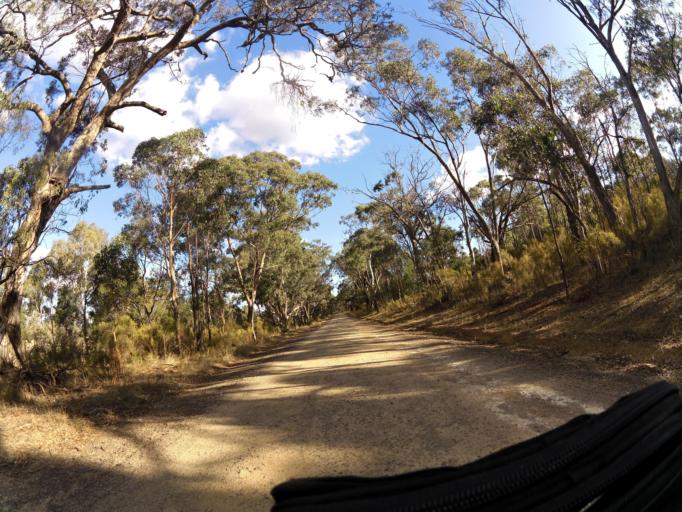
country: AU
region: Victoria
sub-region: Greater Bendigo
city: Kennington
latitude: -37.0118
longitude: 144.8090
